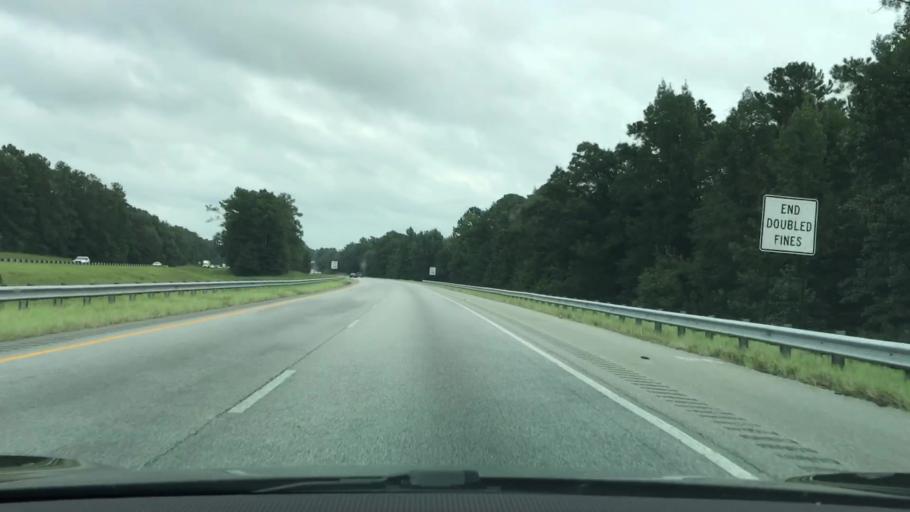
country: US
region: Alabama
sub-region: Lee County
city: Auburn
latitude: 32.5168
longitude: -85.5803
